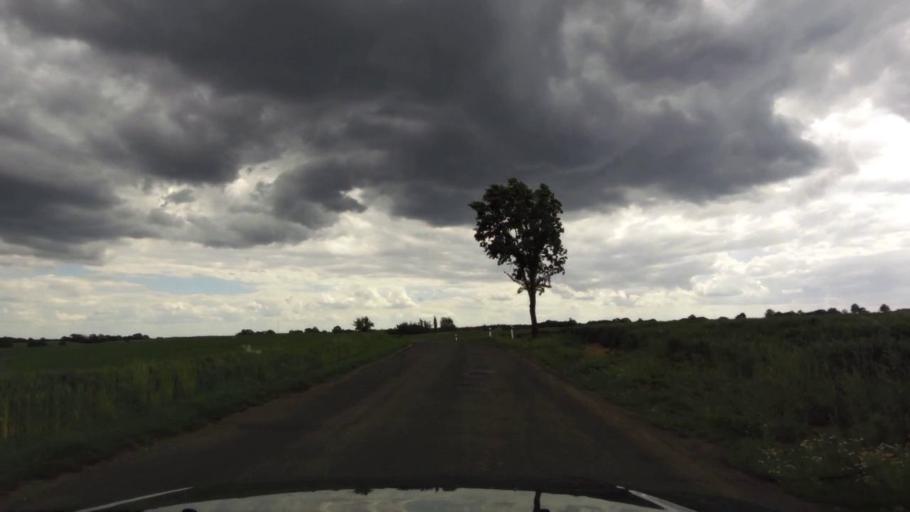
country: PL
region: West Pomeranian Voivodeship
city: Trzcinsko Zdroj
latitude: 52.9217
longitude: 14.5924
